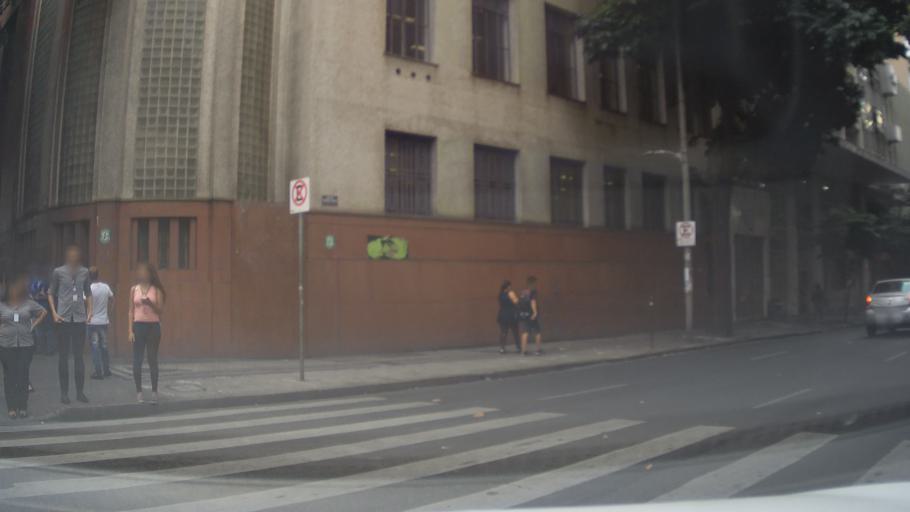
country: BR
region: Minas Gerais
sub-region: Belo Horizonte
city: Belo Horizonte
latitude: -19.9198
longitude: -43.9373
